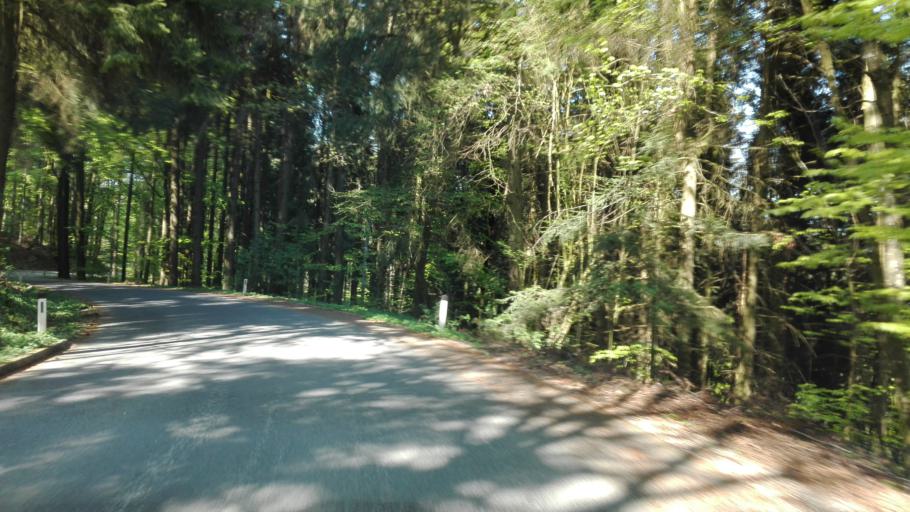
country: AT
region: Upper Austria
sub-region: Politischer Bezirk Rohrbach
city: Atzesberg
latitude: 48.4175
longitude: 13.9181
